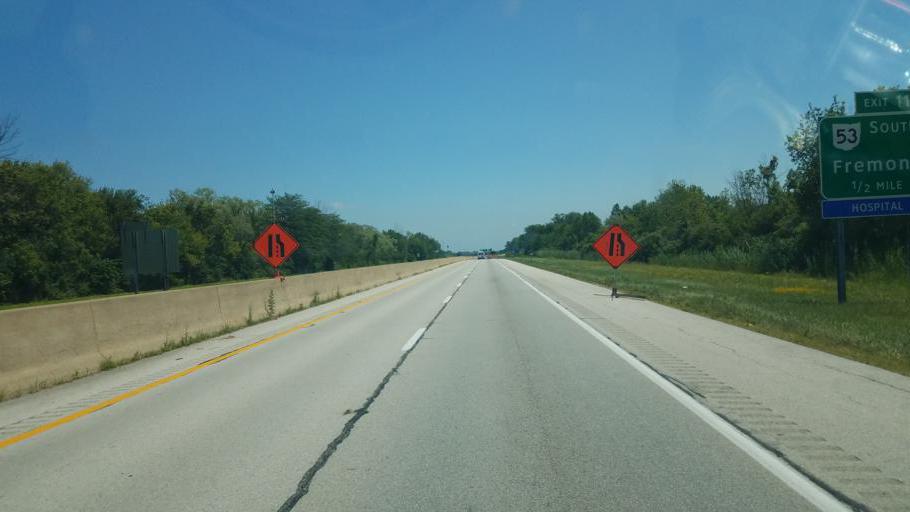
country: US
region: Ohio
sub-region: Ottawa County
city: Port Clinton
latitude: 41.5064
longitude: -82.9815
